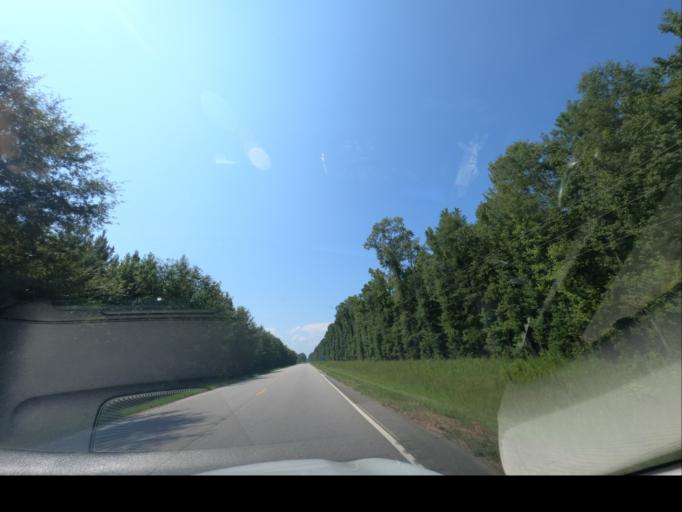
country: US
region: South Carolina
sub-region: Richland County
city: Hopkins
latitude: 33.8763
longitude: -80.9006
